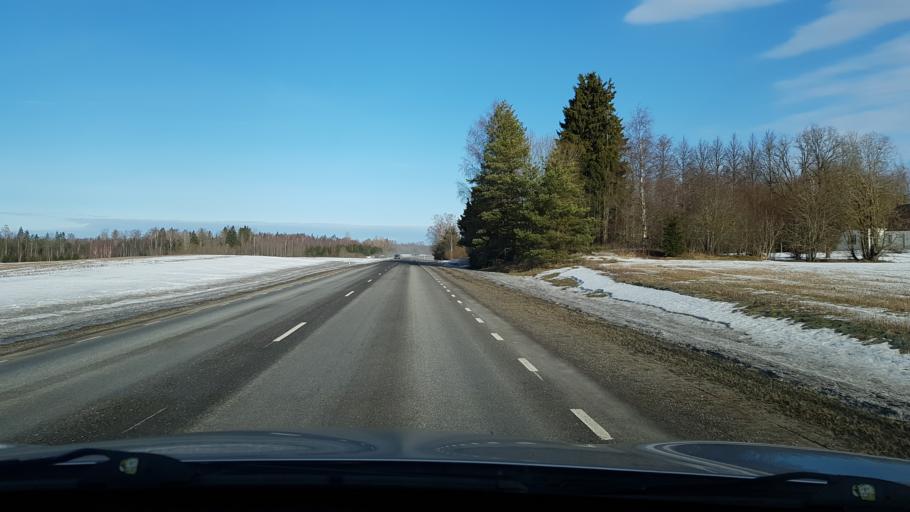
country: EE
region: Viljandimaa
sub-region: Viljandi linn
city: Viljandi
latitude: 58.4269
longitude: 25.5972
